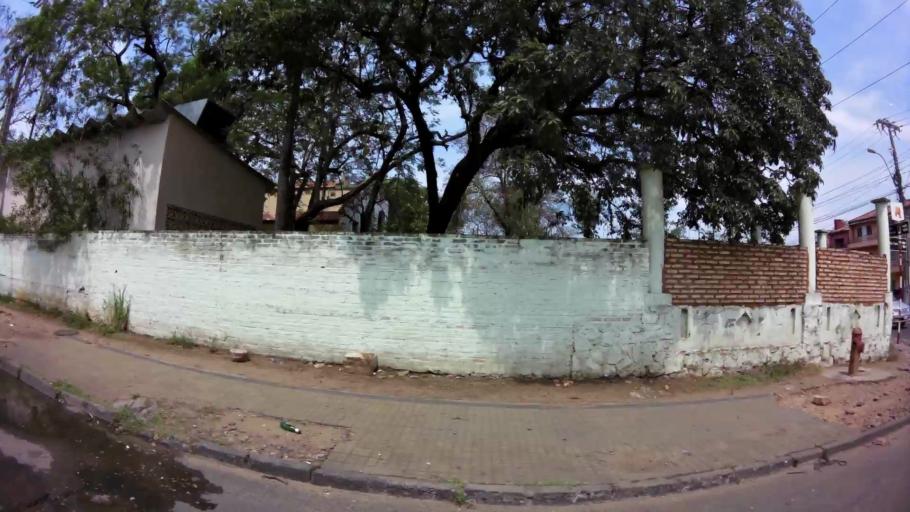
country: PY
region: Asuncion
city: Asuncion
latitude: -25.2571
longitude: -57.5848
